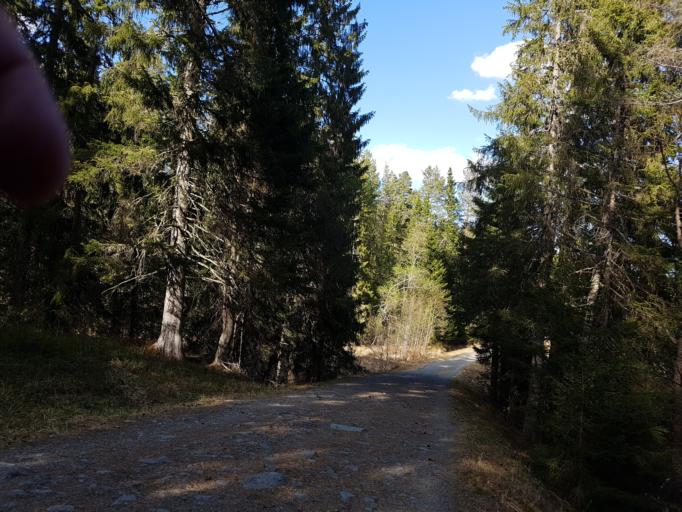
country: NO
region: Sor-Trondelag
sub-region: Trondheim
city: Trondheim
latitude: 63.4383
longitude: 10.3018
